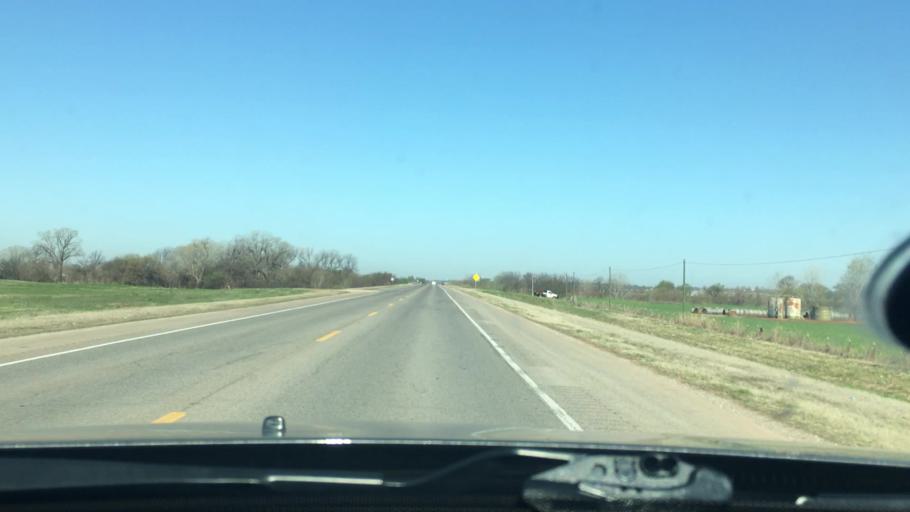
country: US
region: Oklahoma
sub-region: Garvin County
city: Lindsay
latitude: 34.8293
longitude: -97.5690
